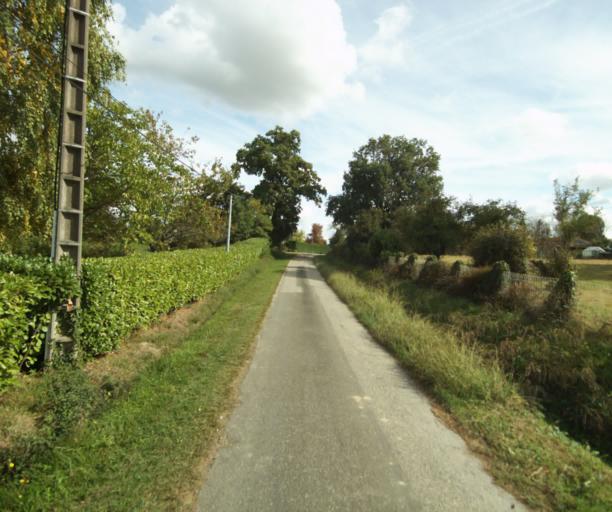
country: FR
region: Midi-Pyrenees
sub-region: Departement du Gers
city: Eauze
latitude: 43.8423
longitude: 0.1516
